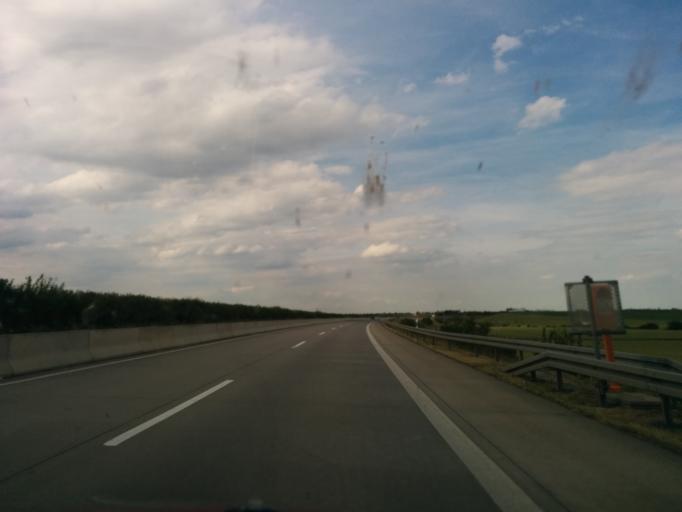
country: DE
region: Thuringia
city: Zimmernsupra
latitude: 50.9888
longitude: 10.9116
